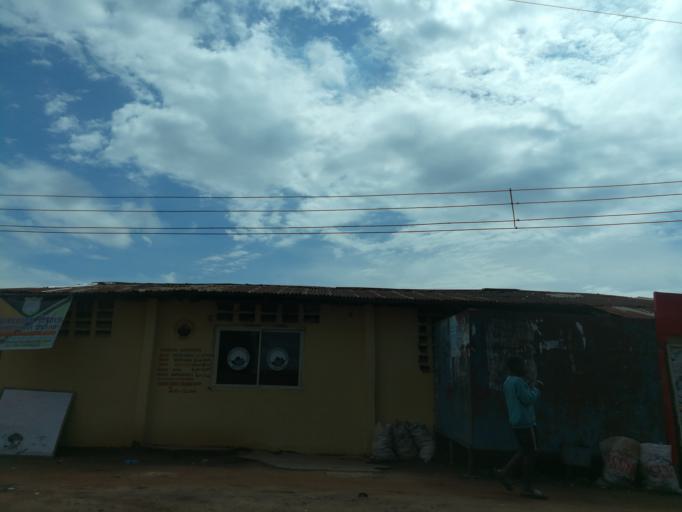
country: NG
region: Lagos
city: Ikorodu
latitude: 6.6049
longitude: 3.5173
